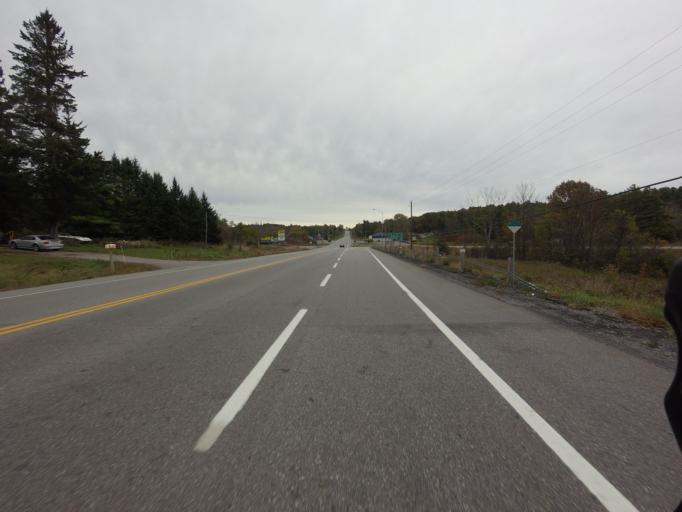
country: CA
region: Ontario
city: Gananoque
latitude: 44.4843
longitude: -76.1956
